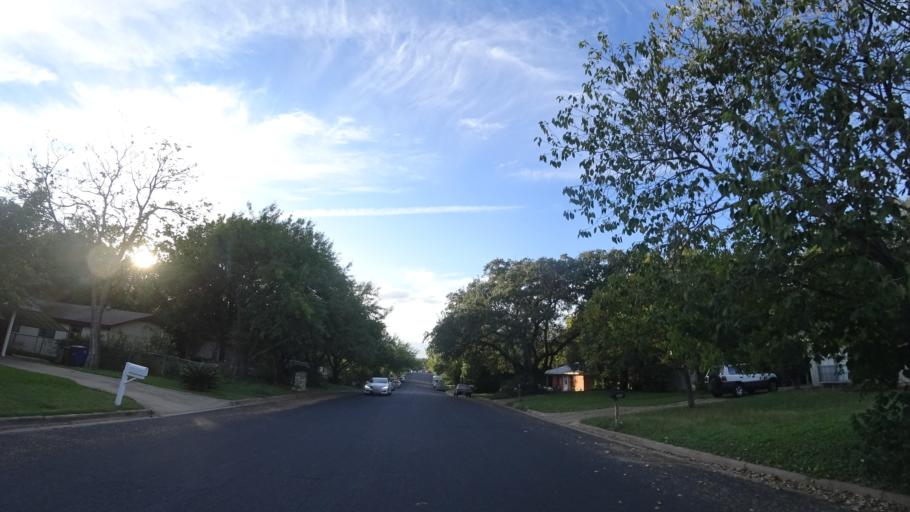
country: US
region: Texas
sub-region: Travis County
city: Austin
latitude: 30.2134
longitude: -97.7645
